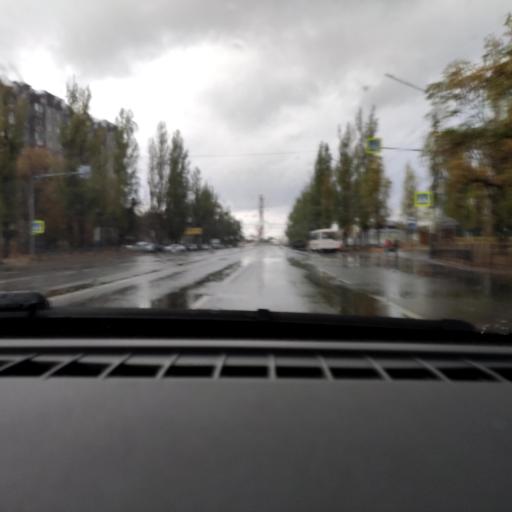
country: RU
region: Voronezj
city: Voronezh
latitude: 51.7042
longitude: 39.2756
